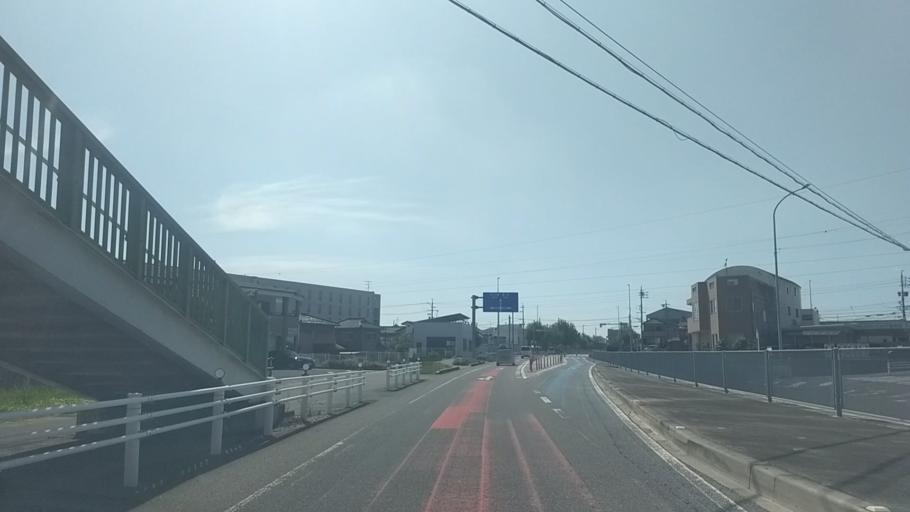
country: JP
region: Aichi
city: Okazaki
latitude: 34.9838
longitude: 137.1327
